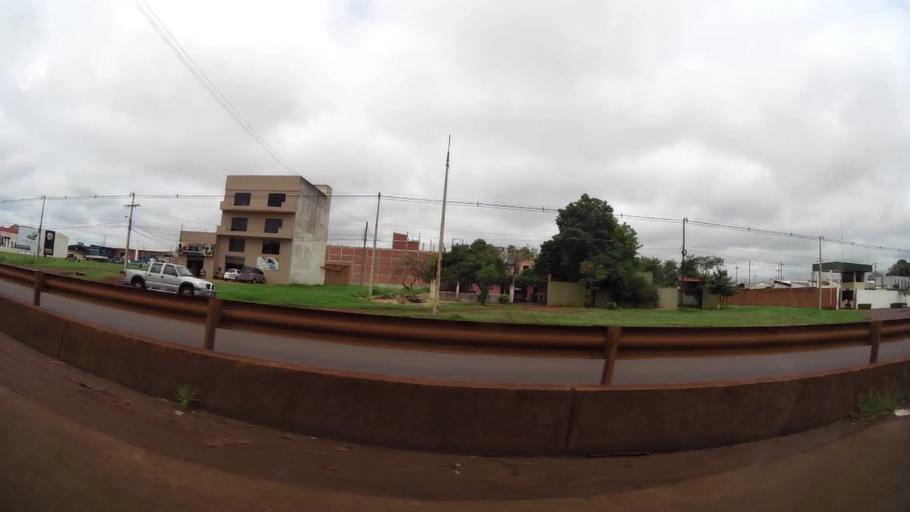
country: PY
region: Alto Parana
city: Presidente Franco
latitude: -25.4915
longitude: -54.7476
